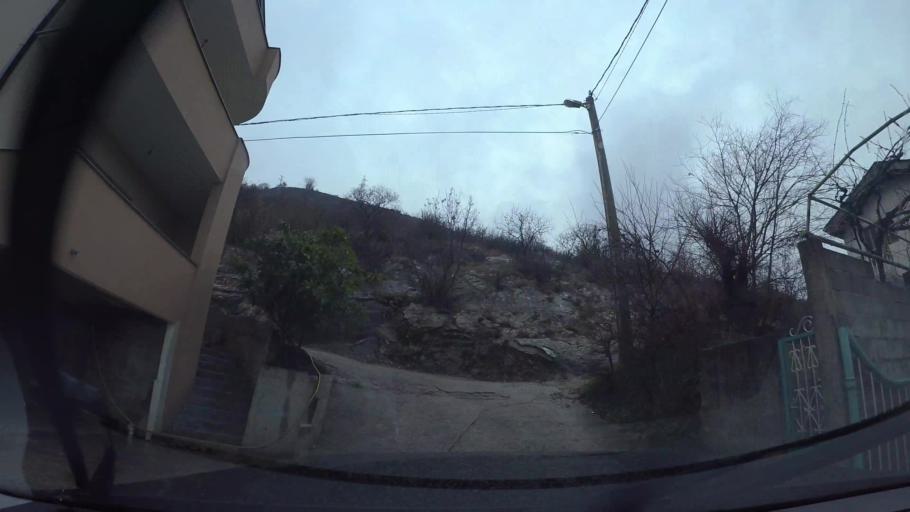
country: BA
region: Federation of Bosnia and Herzegovina
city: Cim
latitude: 43.3562
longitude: 17.7829
